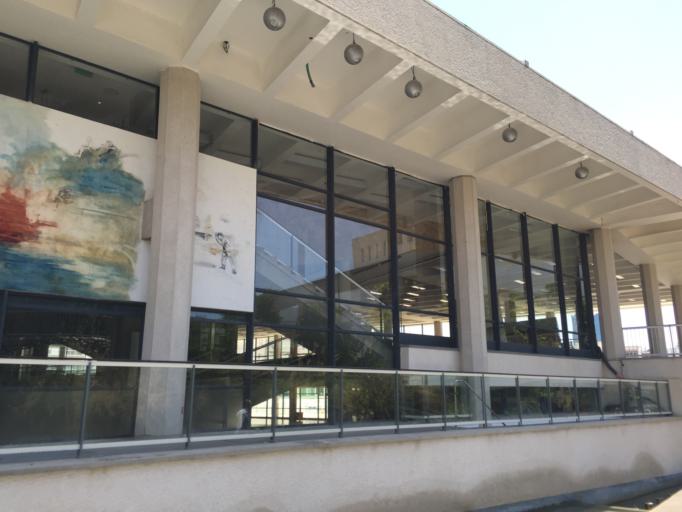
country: IL
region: Tel Aviv
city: Tel Aviv
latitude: 32.0736
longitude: 34.7797
